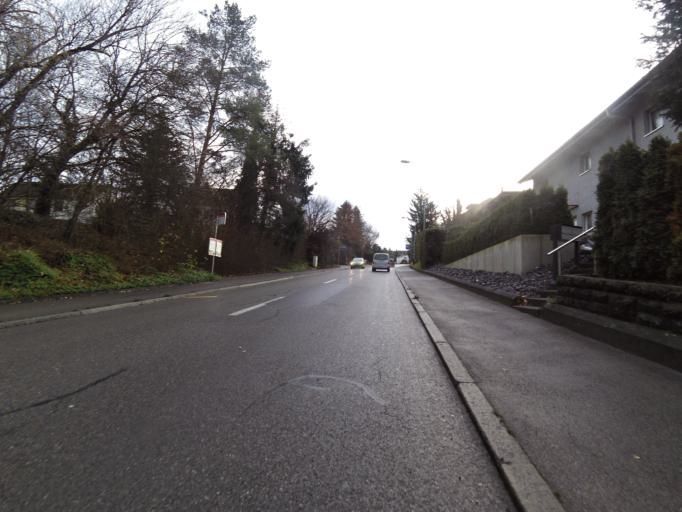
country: CH
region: Thurgau
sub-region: Frauenfeld District
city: Frauenfeld
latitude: 47.5507
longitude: 8.9043
